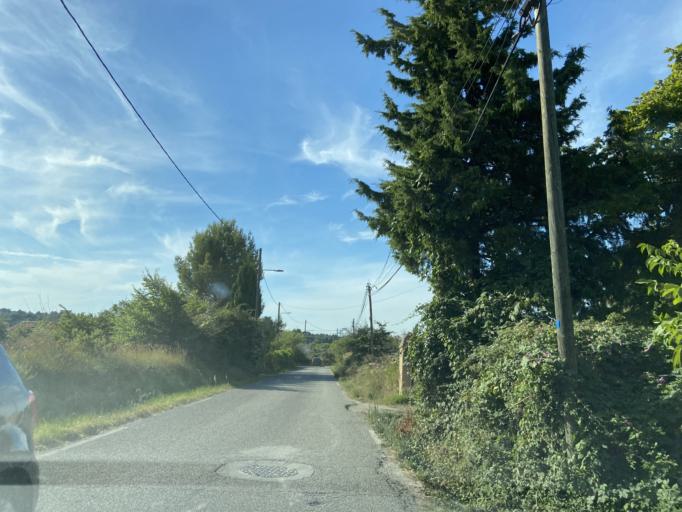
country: FR
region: Provence-Alpes-Cote d'Azur
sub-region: Departement des Bouches-du-Rhone
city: Saint-Chamas
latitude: 43.5664
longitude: 5.0202
